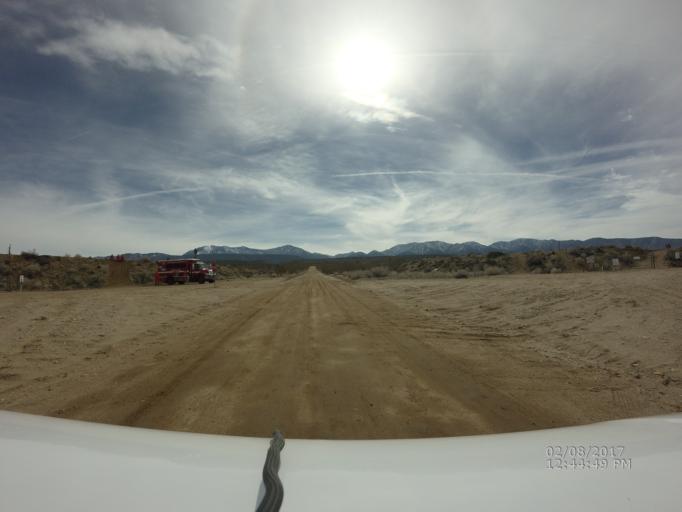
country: US
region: California
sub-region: Los Angeles County
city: Lake Los Angeles
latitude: 34.4806
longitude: -117.8178
